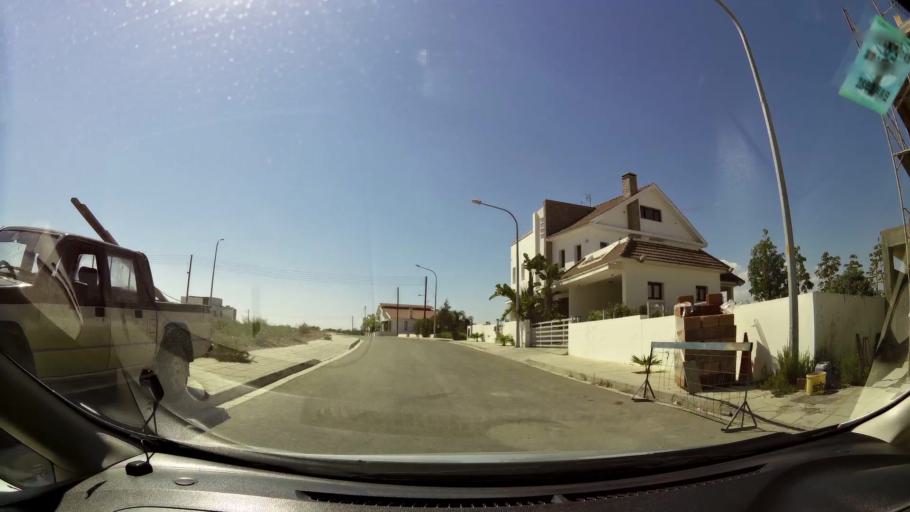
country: CY
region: Larnaka
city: Livadia
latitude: 34.9548
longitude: 33.6364
